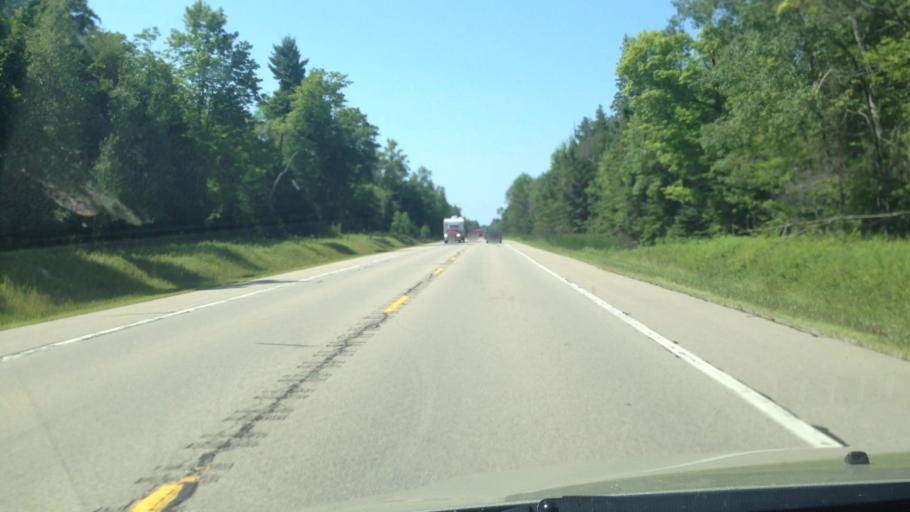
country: US
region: Michigan
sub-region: Menominee County
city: Menominee
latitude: 45.4015
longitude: -87.3636
